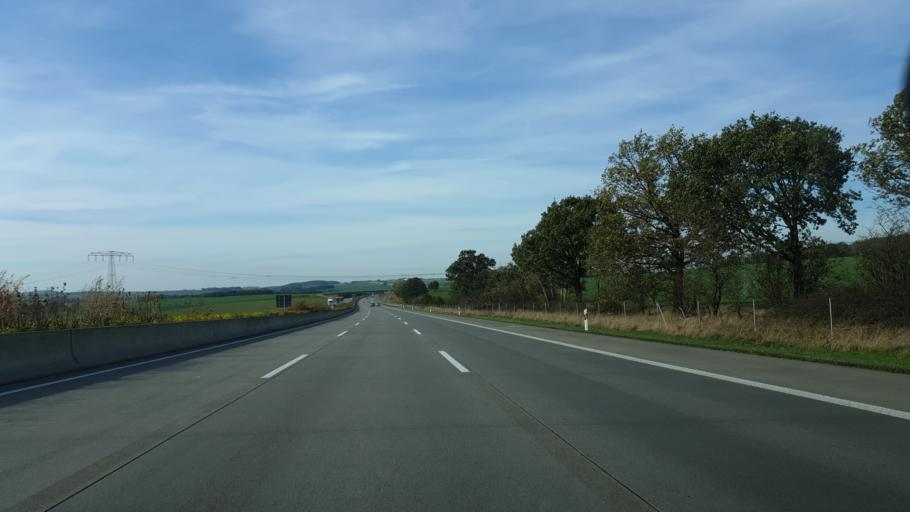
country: DE
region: Thuringia
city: Vollmershain
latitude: 50.8617
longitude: 12.2985
